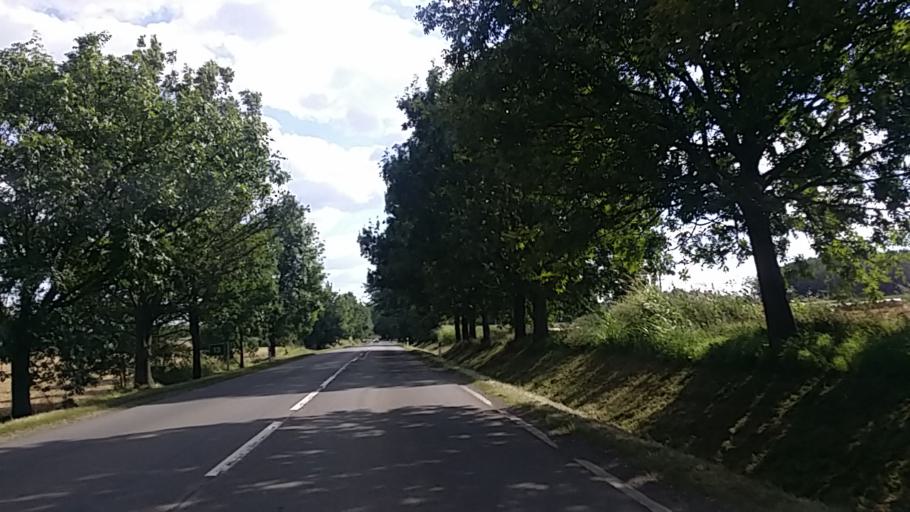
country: HU
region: Baranya
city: Sasd
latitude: 46.2761
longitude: 18.1063
